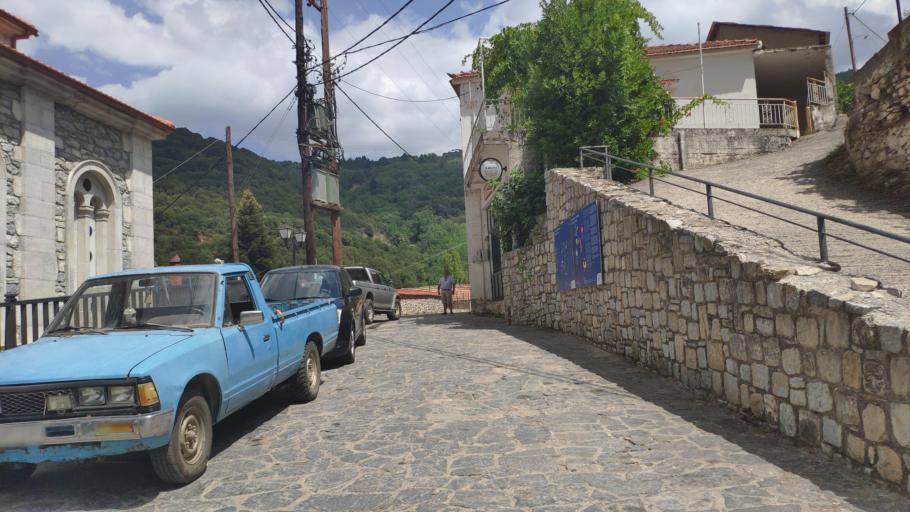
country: GR
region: Peloponnese
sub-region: Nomos Lakonias
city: Kariai
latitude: 37.2454
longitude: 22.5518
